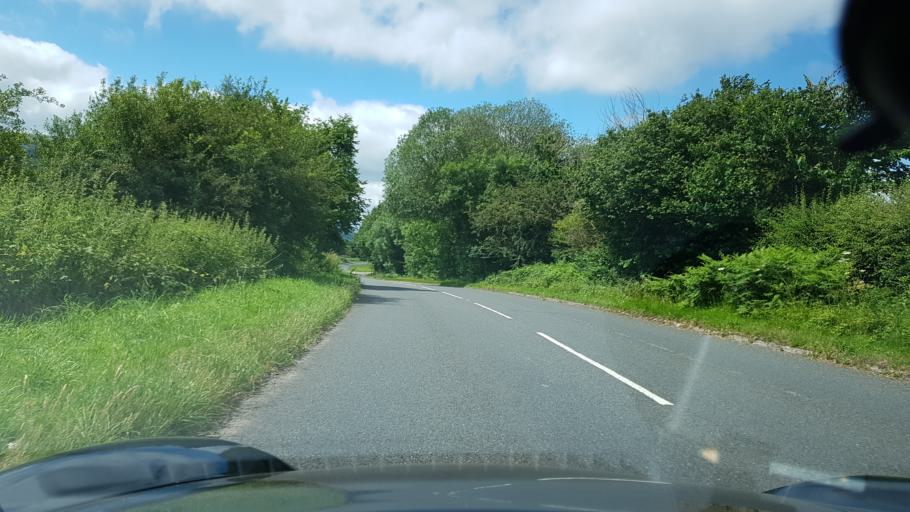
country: GB
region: Wales
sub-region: Monmouthshire
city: Abergavenny
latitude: 51.7893
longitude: -2.9856
